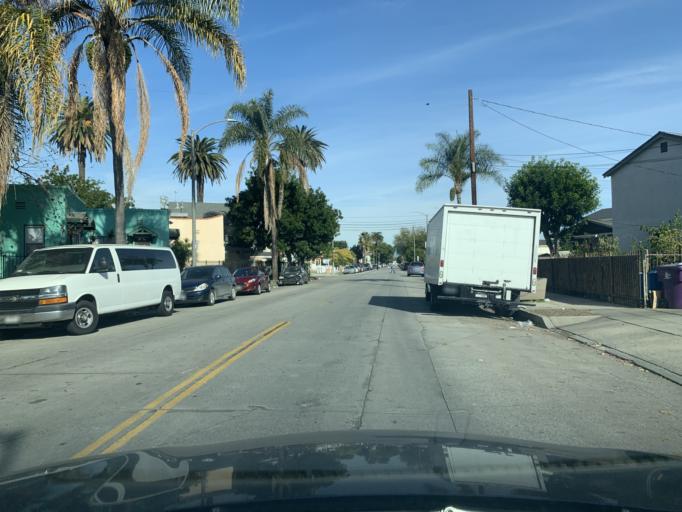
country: US
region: California
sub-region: Los Angeles County
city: East Rancho Dominguez
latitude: 33.8545
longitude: -118.1947
